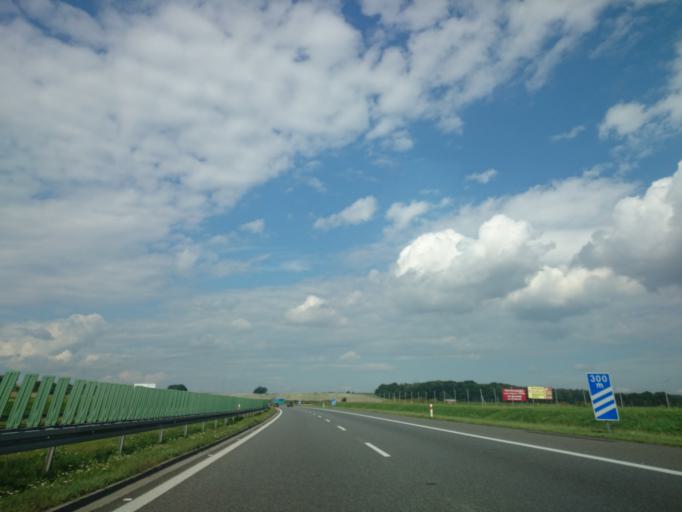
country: PL
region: Opole Voivodeship
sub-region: Powiat strzelecki
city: Strzelce Opolskie
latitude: 50.4586
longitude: 18.2821
